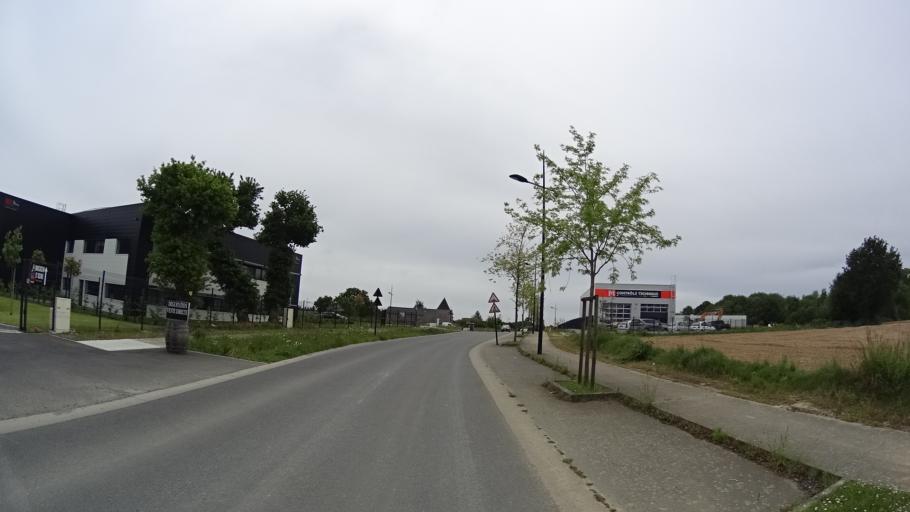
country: FR
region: Brittany
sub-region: Departement d'Ille-et-Vilaine
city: Pace
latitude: 48.1415
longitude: -1.7595
